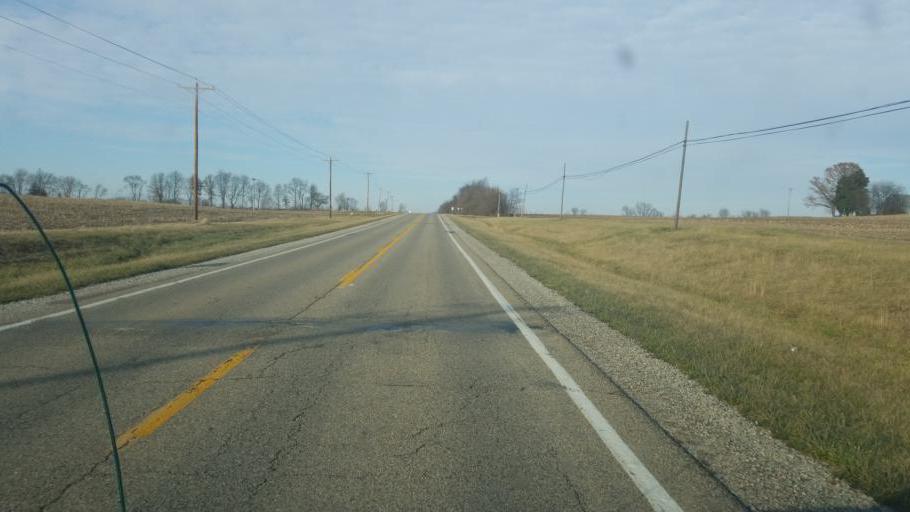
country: US
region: Illinois
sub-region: Lawrence County
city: Bridgeport
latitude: 38.6255
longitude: -87.6940
